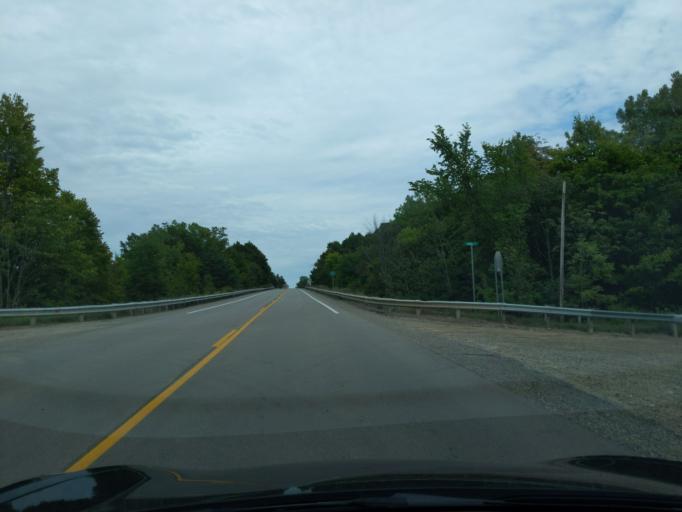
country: US
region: Michigan
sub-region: Barry County
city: Nashville
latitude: 42.5673
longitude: -85.0750
